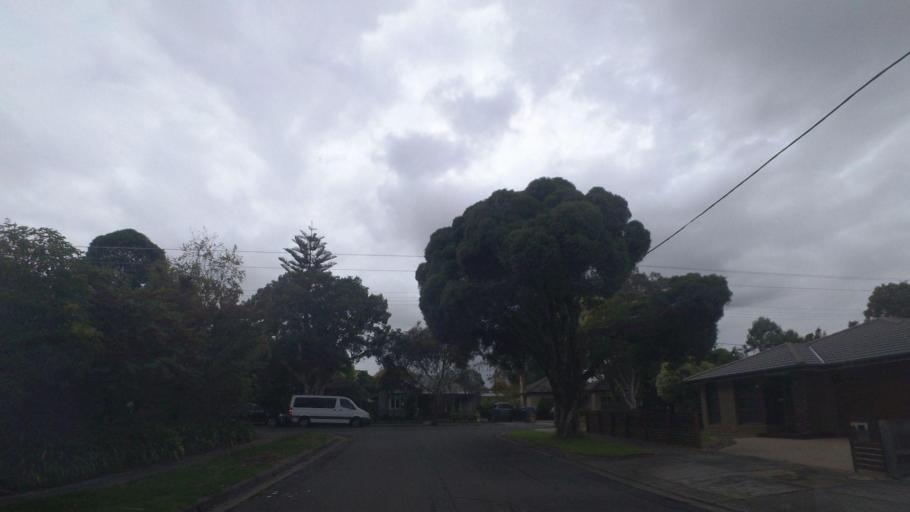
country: AU
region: Victoria
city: Forest Hill
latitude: -37.8324
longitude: 145.1761
